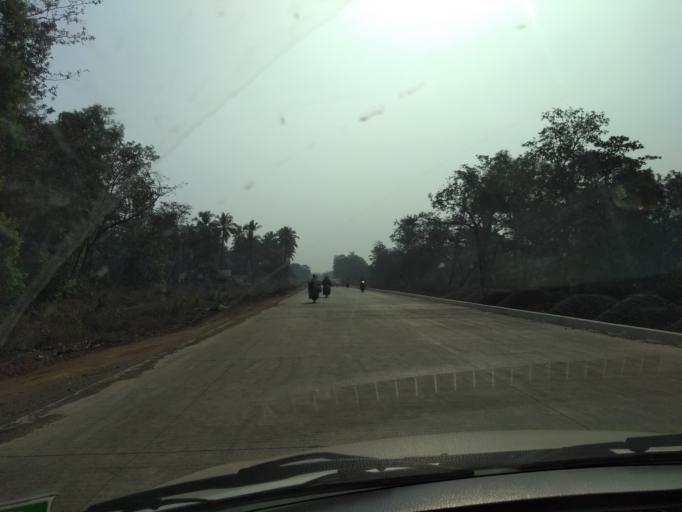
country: IN
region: Maharashtra
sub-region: Sindhudurg
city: Kudal
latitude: 15.9692
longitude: 73.7229
